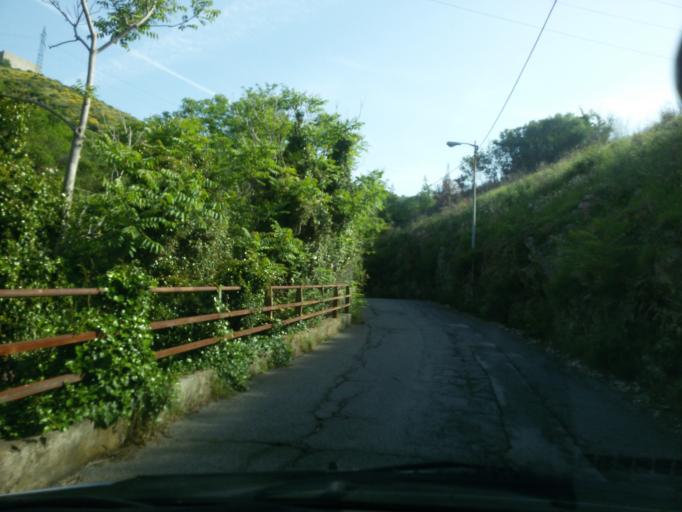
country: IT
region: Liguria
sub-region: Provincia di Genova
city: Genoa
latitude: 44.4278
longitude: 8.9160
